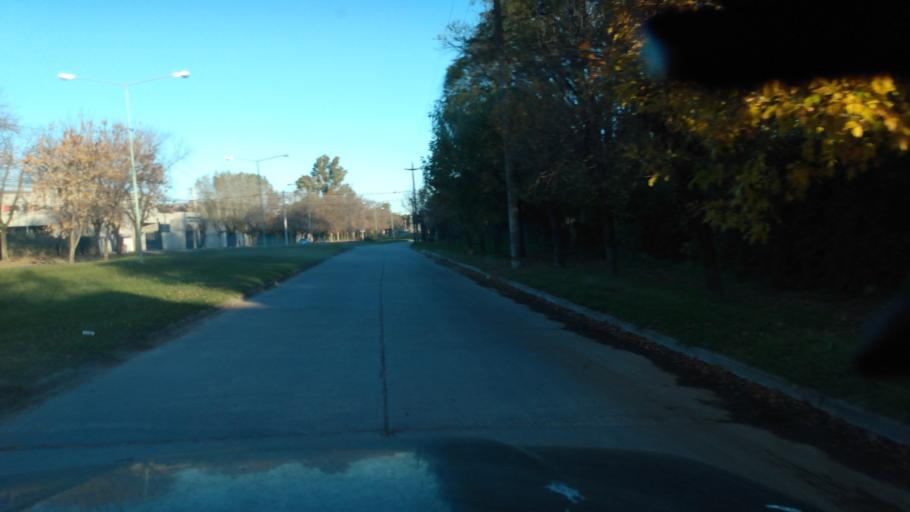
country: AR
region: Buenos Aires
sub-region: Partido de Lujan
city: Lujan
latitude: -34.5615
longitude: -59.1272
